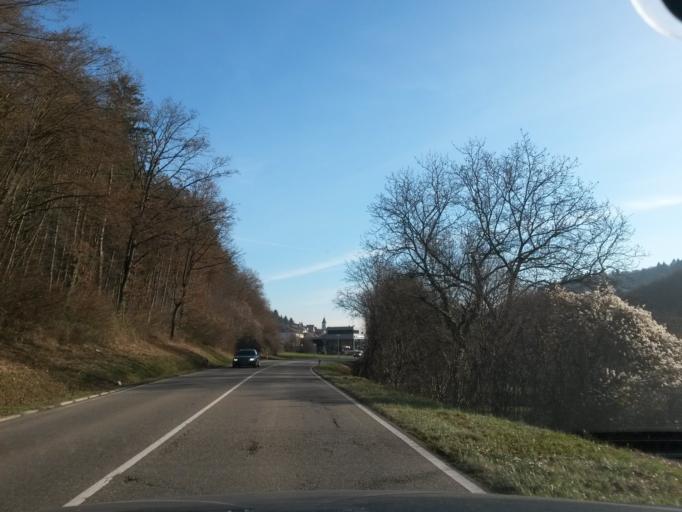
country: DE
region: Baden-Wuerttemberg
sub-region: Karlsruhe Region
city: Ispringen
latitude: 48.9230
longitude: 8.6571
